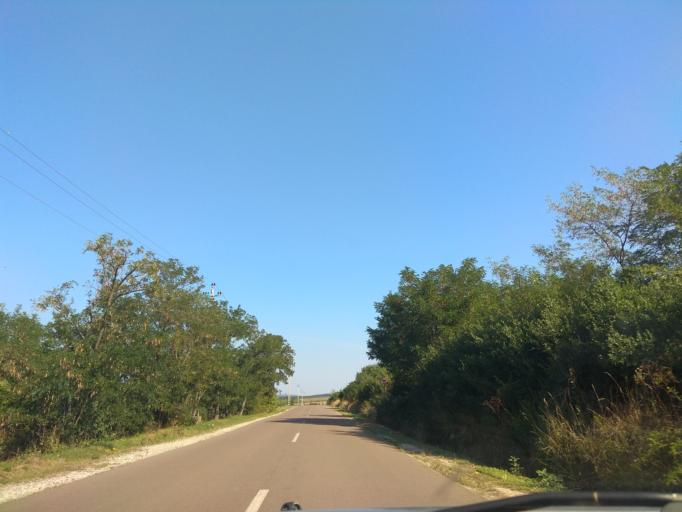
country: HU
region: Borsod-Abauj-Zemplen
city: Nyekladhaza
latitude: 47.9713
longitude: 20.7968
